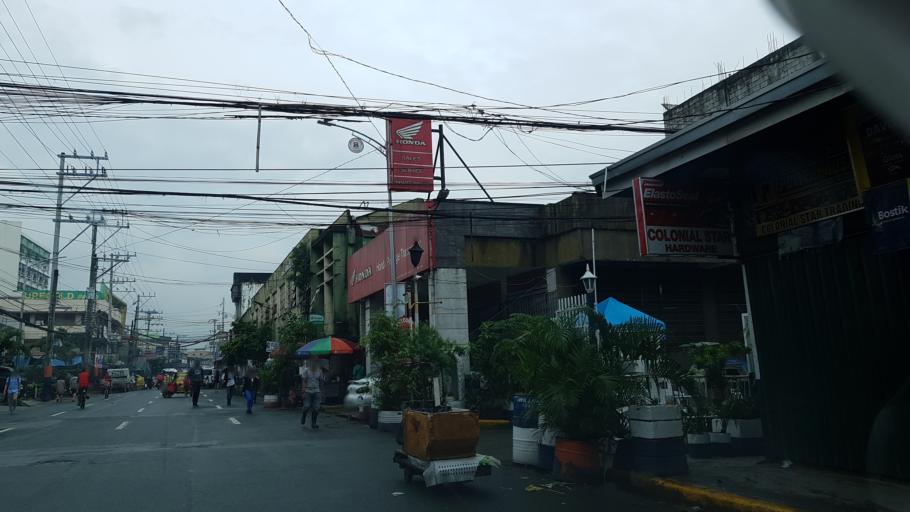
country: PH
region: Metro Manila
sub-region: City of Manila
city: Quiapo
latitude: 14.5757
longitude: 120.9942
